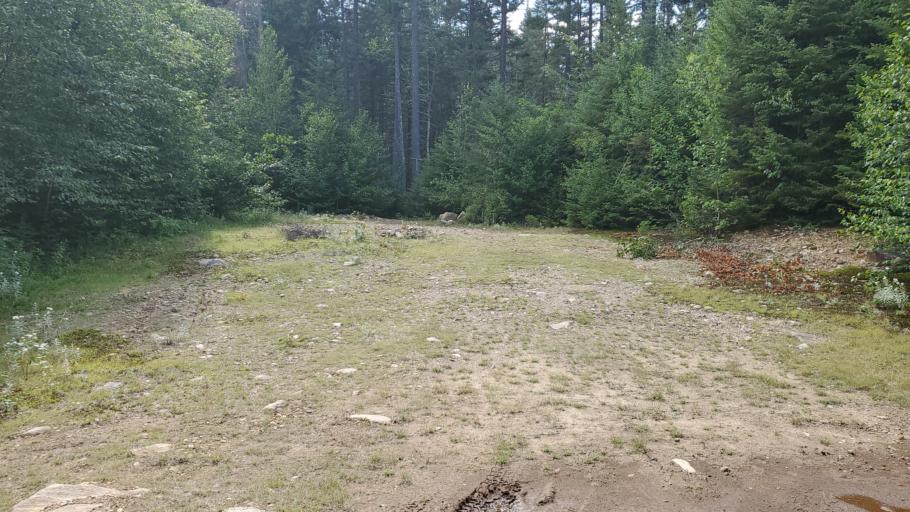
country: CA
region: Quebec
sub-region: Laurentides
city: Val-David
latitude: 46.3877
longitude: -74.1482
